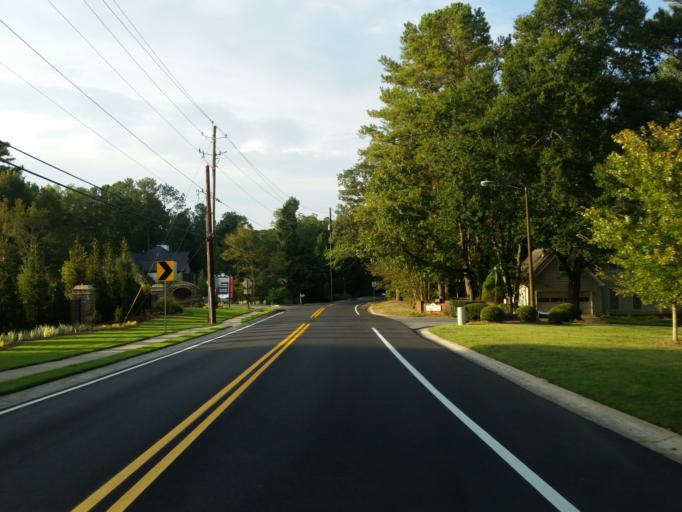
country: US
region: Georgia
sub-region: Cobb County
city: Marietta
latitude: 33.9986
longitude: -84.4639
